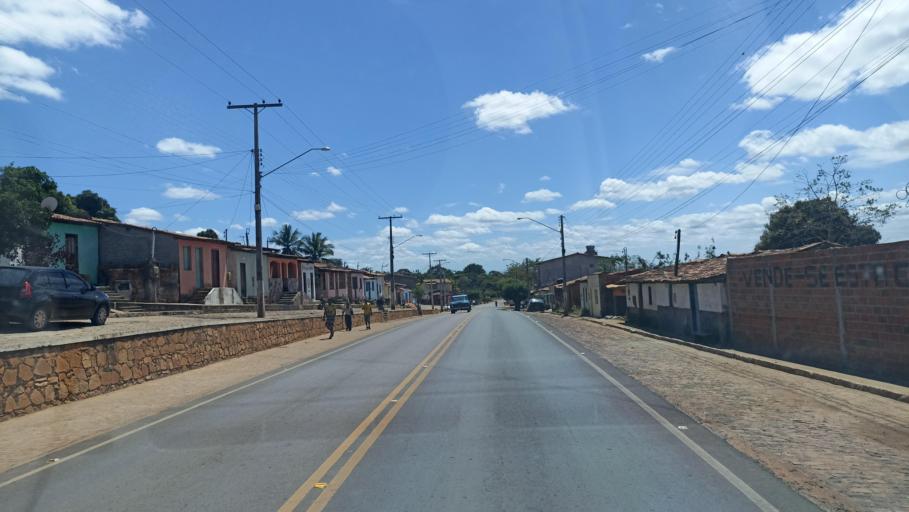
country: BR
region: Bahia
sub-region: Andarai
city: Vera Cruz
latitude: -12.7939
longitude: -41.3281
